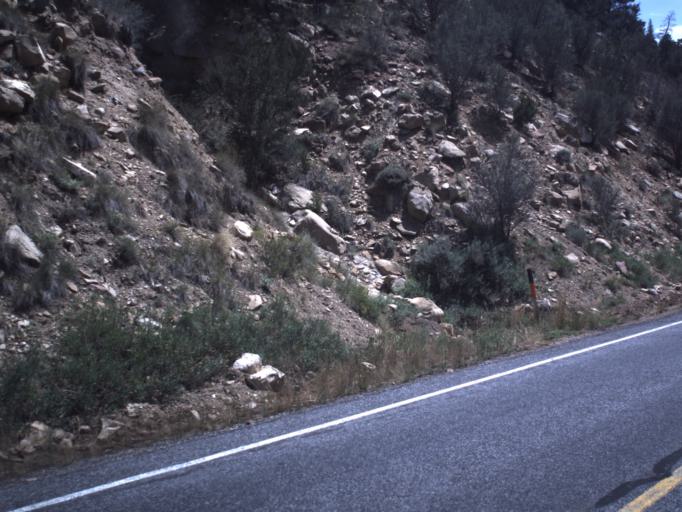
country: US
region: Utah
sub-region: Emery County
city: Huntington
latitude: 39.4309
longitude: -111.1300
